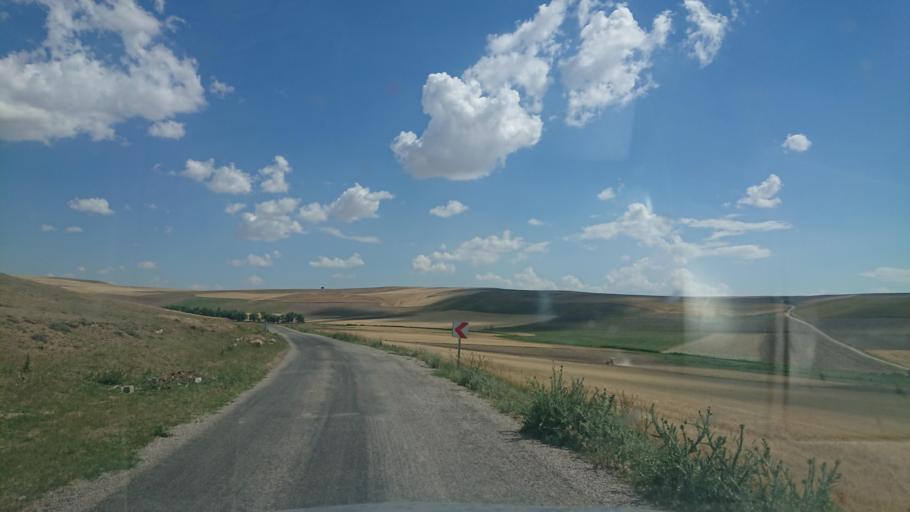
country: TR
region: Aksaray
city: Agacoren
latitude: 38.8227
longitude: 33.7902
